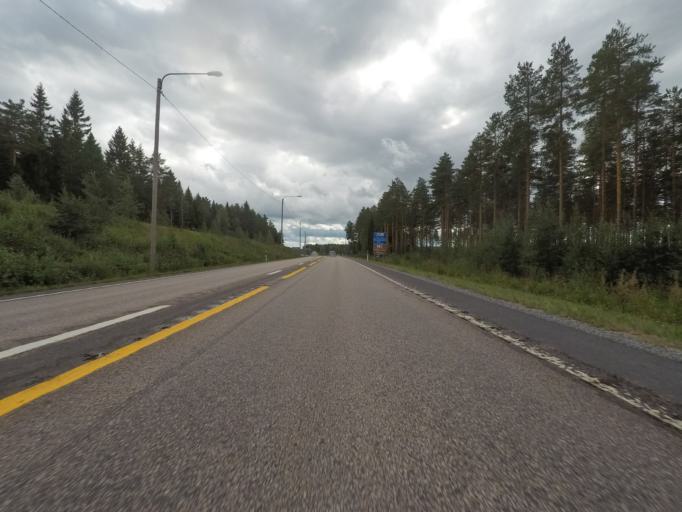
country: FI
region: Paijanne Tavastia
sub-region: Lahti
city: Hartola
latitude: 61.5699
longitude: 26.0044
